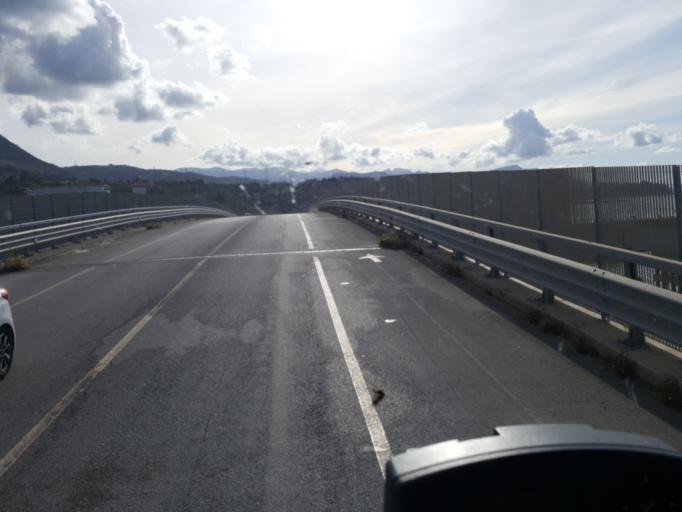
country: IT
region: Sicily
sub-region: Palermo
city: Sciara
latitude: 37.9706
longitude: 13.7542
